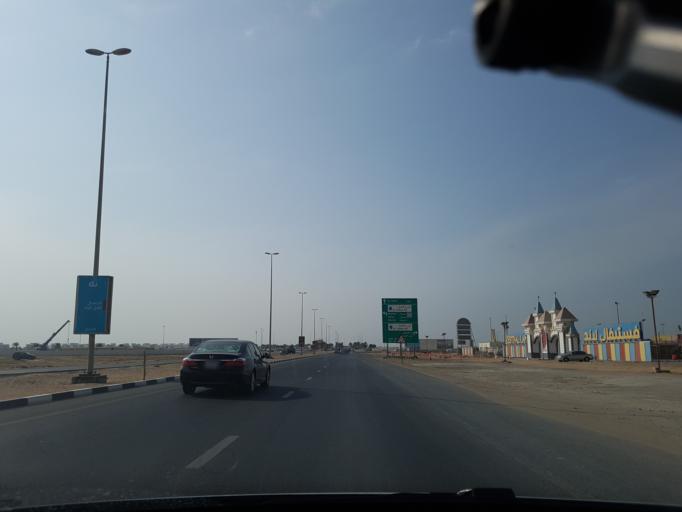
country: AE
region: Ajman
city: Ajman
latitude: 25.4331
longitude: 55.5076
